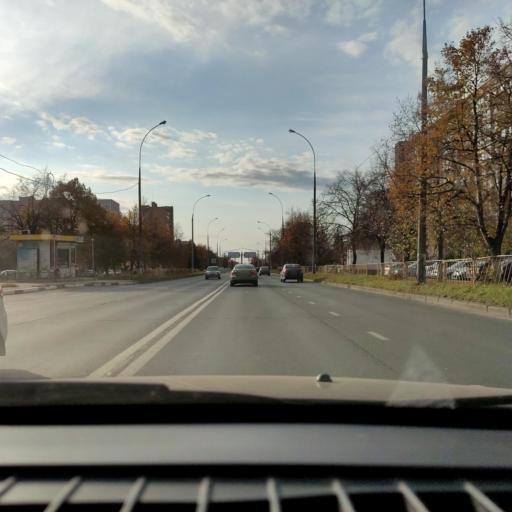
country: RU
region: Samara
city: Tol'yatti
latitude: 53.5288
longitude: 49.3124
